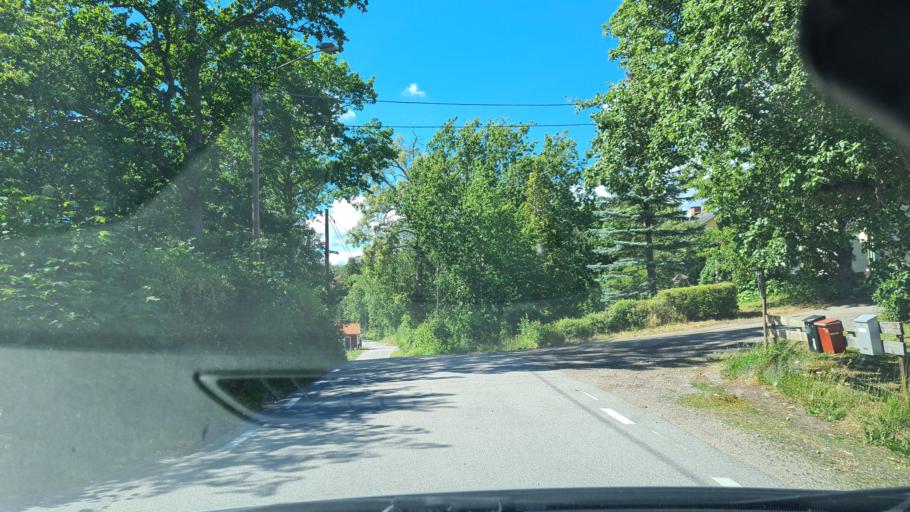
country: SE
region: OEstergoetland
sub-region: Norrkopings Kommun
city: Krokek
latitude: 58.6620
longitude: 16.4190
